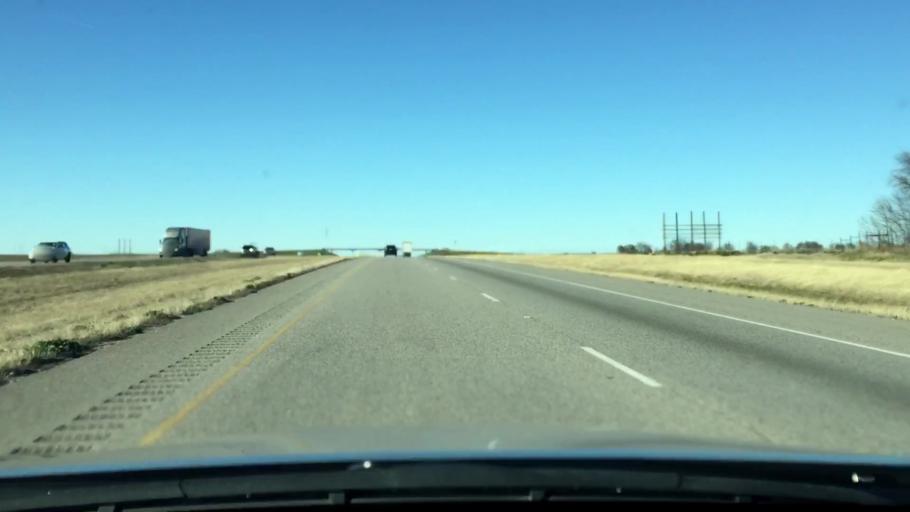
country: US
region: Texas
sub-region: Hill County
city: Itasca
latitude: 32.1194
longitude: -97.1158
